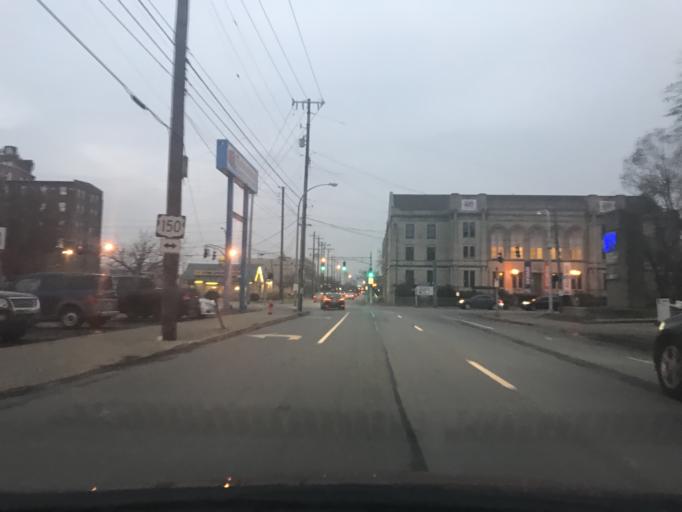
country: US
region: Kentucky
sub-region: Jefferson County
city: Louisville
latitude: 38.2458
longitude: -85.7475
